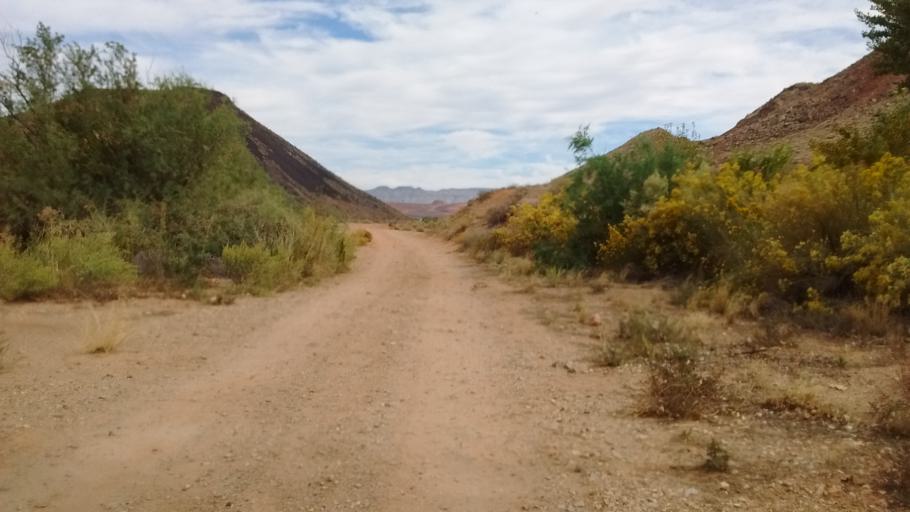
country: US
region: Utah
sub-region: Washington County
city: Washington
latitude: 37.1229
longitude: -113.4913
